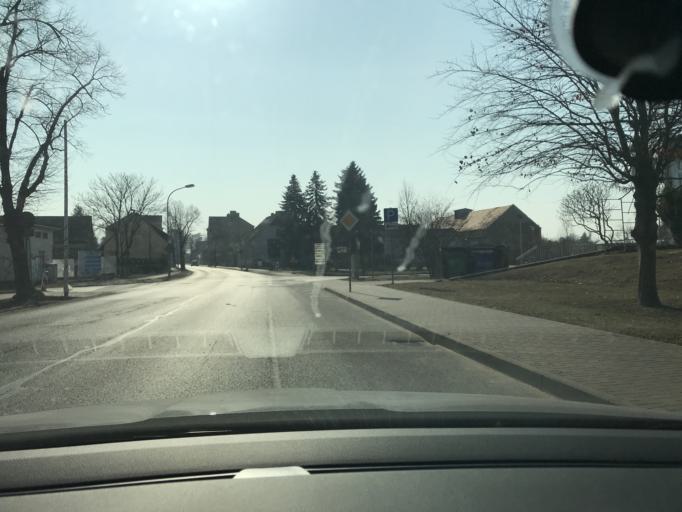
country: DE
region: Brandenburg
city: Mittenwalde
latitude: 52.2701
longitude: 13.5364
